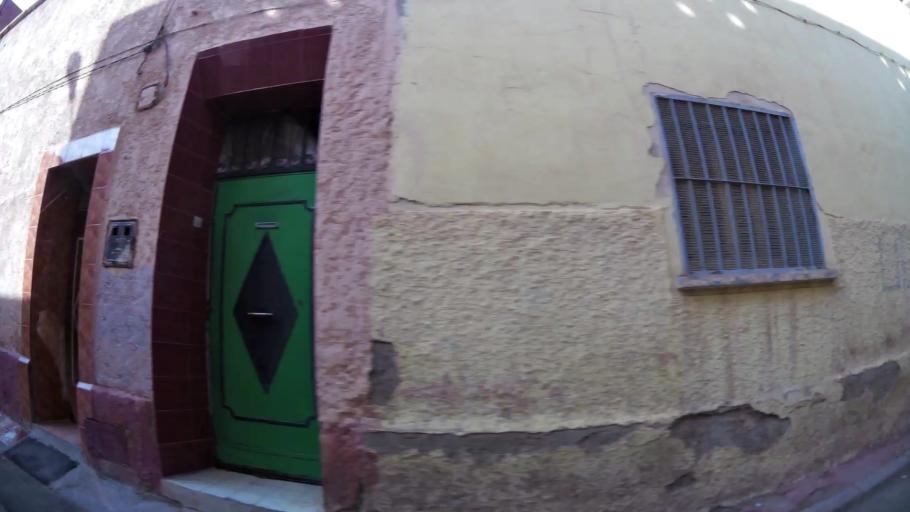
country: MA
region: Oriental
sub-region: Oujda-Angad
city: Oujda
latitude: 34.6870
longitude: -1.9076
